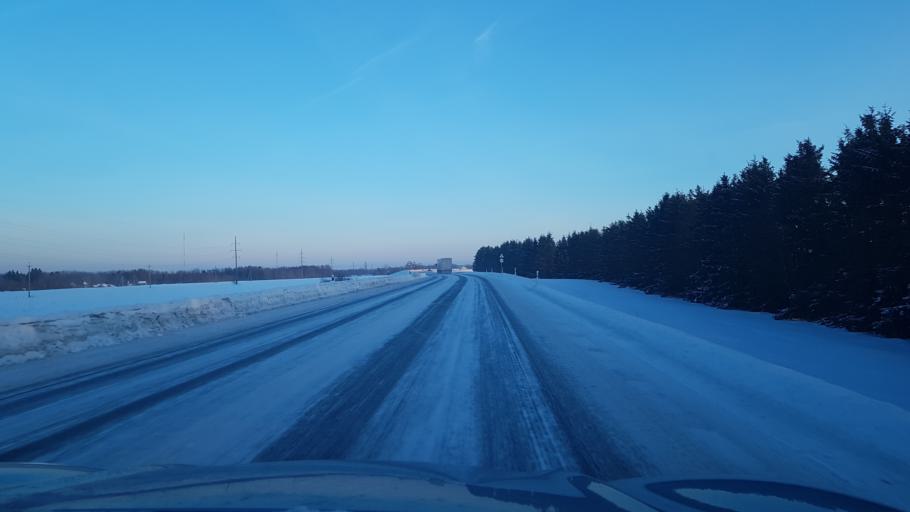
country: EE
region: Ida-Virumaa
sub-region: Narva-Joesuu linn
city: Narva-Joesuu
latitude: 59.4053
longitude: 28.0446
